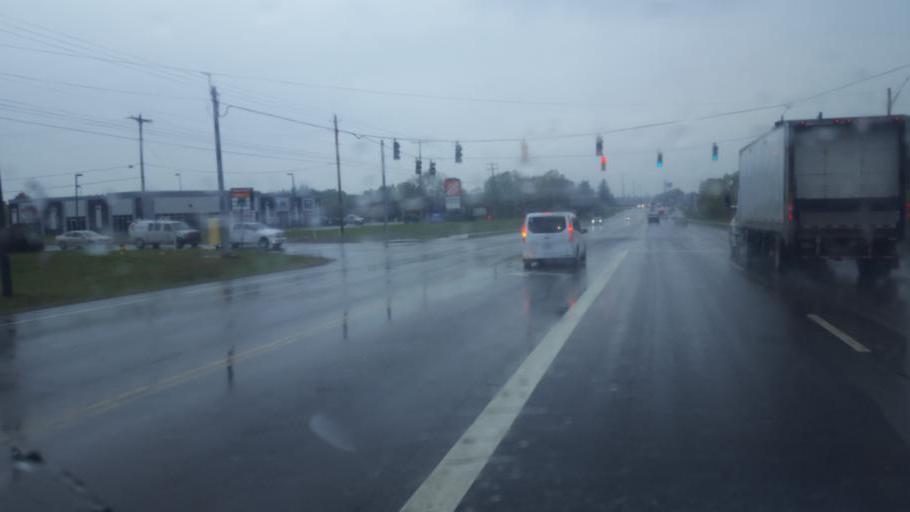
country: US
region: Ohio
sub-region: Ashland County
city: Ashland
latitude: 40.8621
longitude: -82.2820
